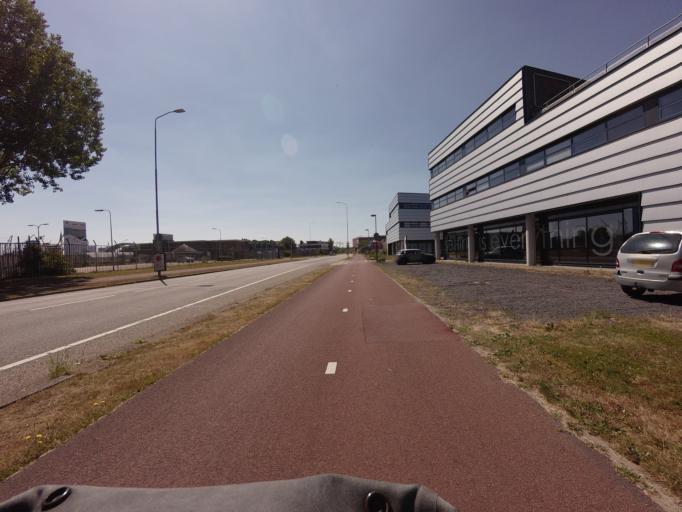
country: NL
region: Utrecht
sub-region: Stichtse Vecht
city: Maarssen
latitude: 52.1021
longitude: 5.0686
